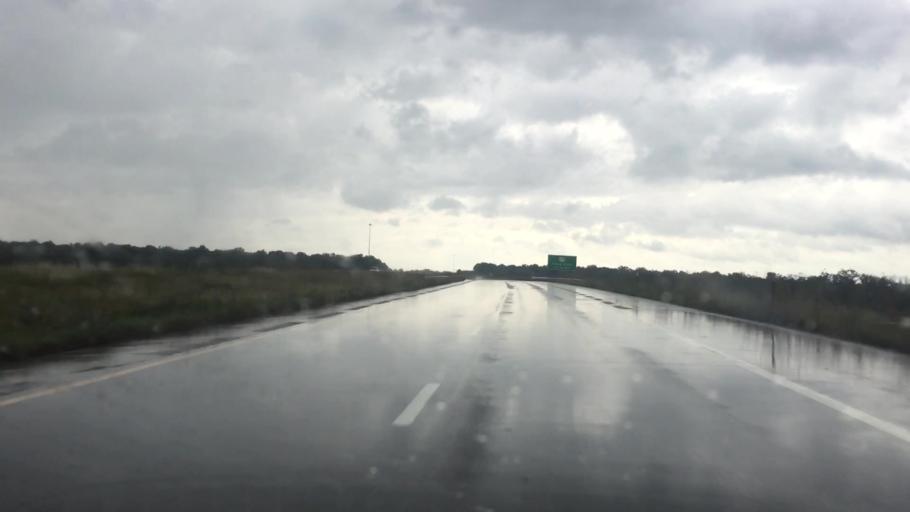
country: US
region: Kansas
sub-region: Miami County
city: Osawatomie
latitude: 38.4981
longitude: -94.9355
